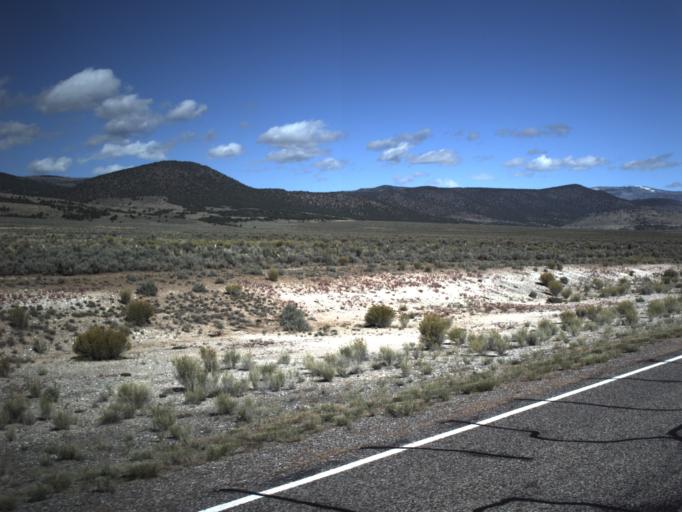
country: US
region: Utah
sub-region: Wayne County
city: Loa
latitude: 38.3964
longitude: -111.9309
